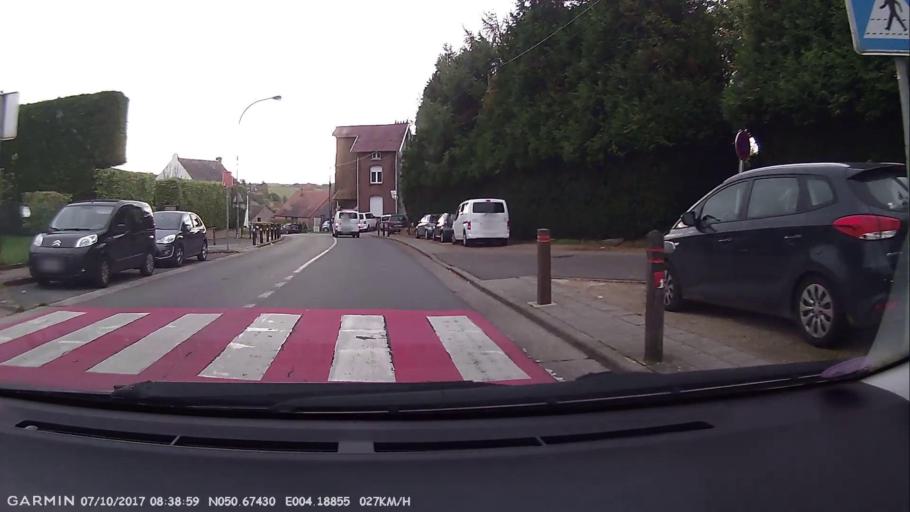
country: BE
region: Wallonia
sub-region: Province du Brabant Wallon
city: Tubize
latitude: 50.6742
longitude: 4.1887
